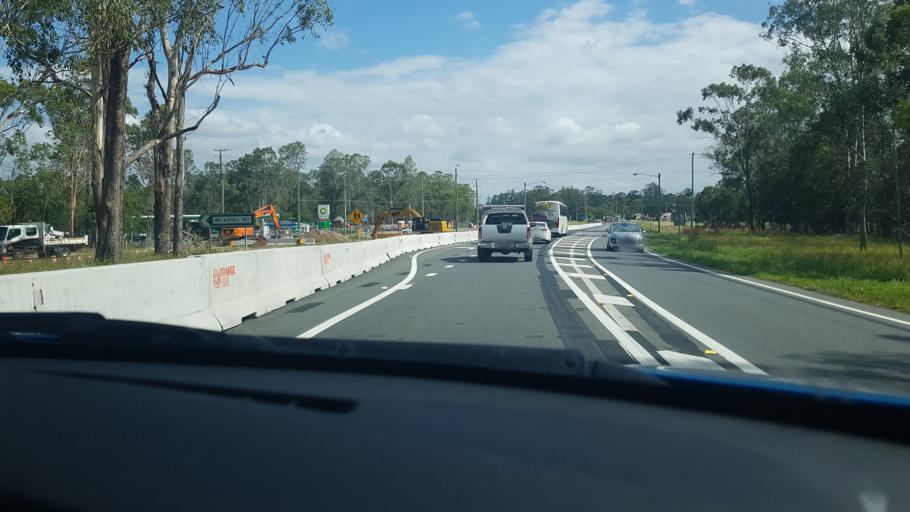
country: AU
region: Queensland
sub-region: Logan
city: North Maclean
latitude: -27.7741
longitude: 153.0144
